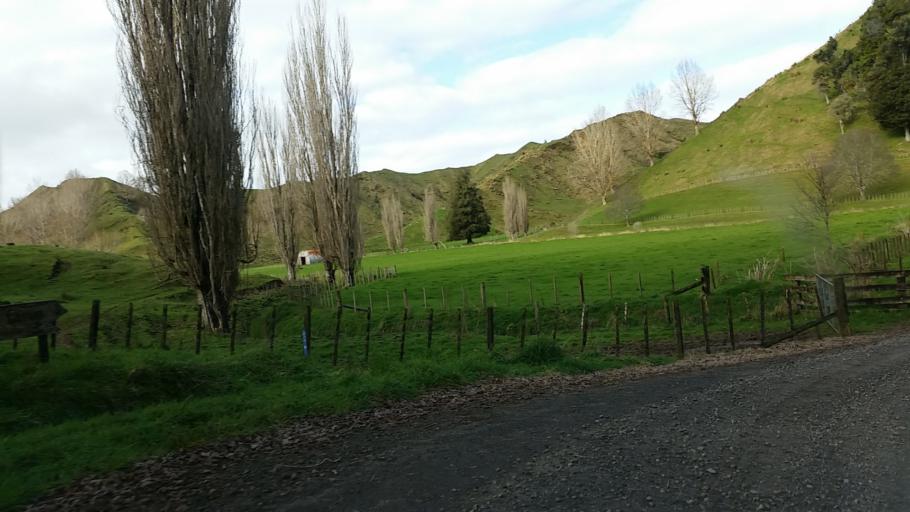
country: NZ
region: Taranaki
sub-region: South Taranaki District
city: Eltham
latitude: -39.2509
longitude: 174.5428
